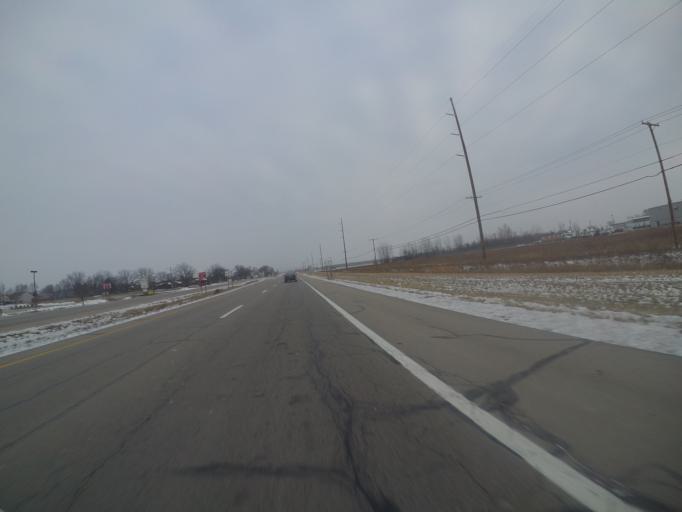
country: US
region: Ohio
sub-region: Wood County
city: Walbridge
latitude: 41.5637
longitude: -83.5365
